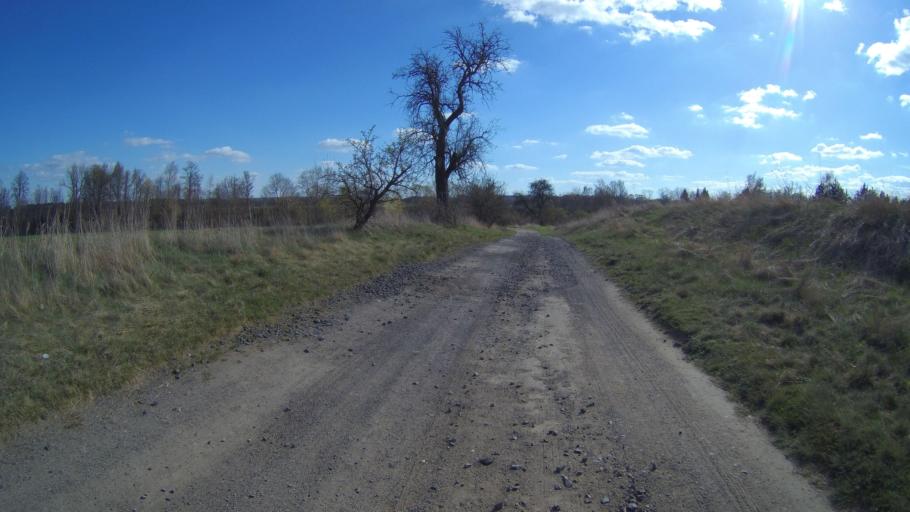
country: CZ
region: Ustecky
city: Brezno
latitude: 50.3595
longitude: 13.4700
